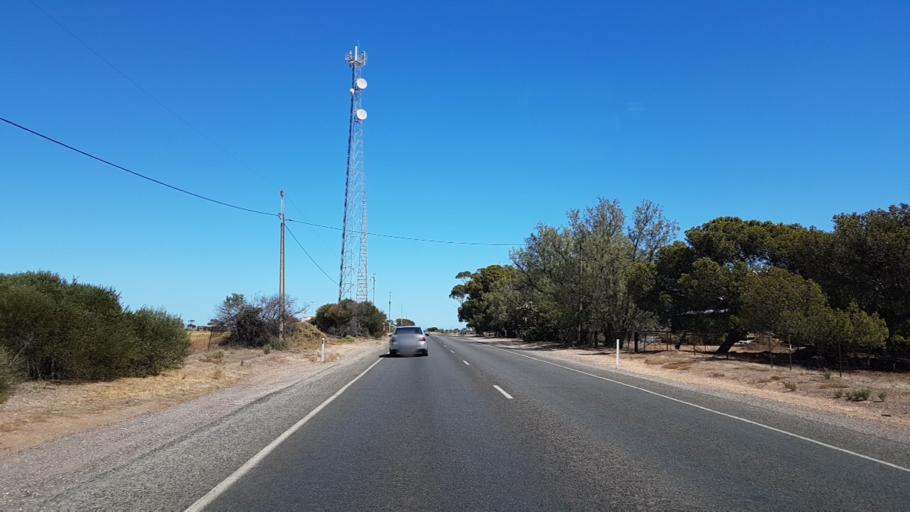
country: AU
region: South Australia
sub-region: Copper Coast
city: Wallaroo
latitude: -33.9489
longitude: 137.6720
